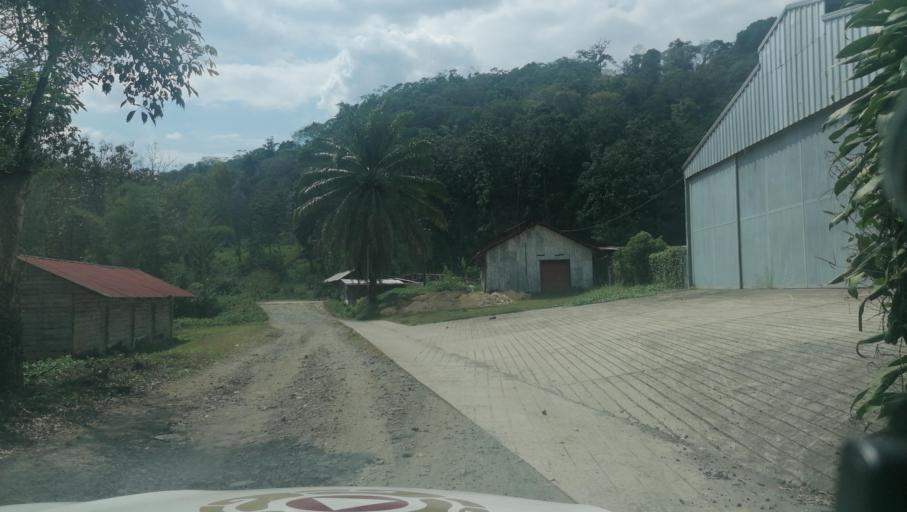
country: MX
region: Chiapas
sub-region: Cacahoatan
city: Benito Juarez
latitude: 15.0279
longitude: -92.2361
